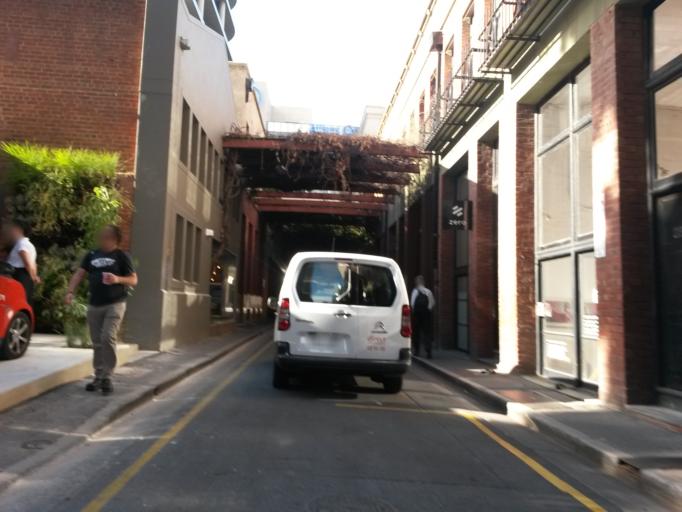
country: AU
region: South Australia
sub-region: Adelaide
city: Adelaide
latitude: -34.9248
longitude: 138.6032
